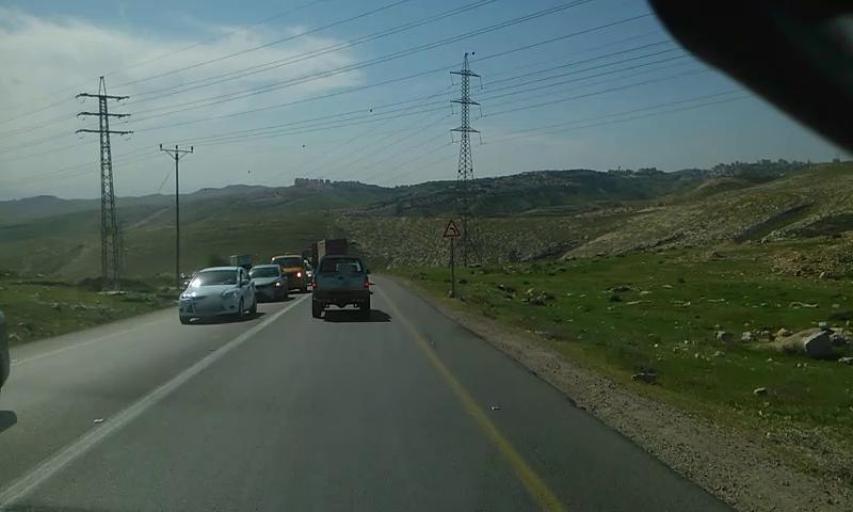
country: PS
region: West Bank
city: `Anata
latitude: 31.8146
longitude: 35.2962
